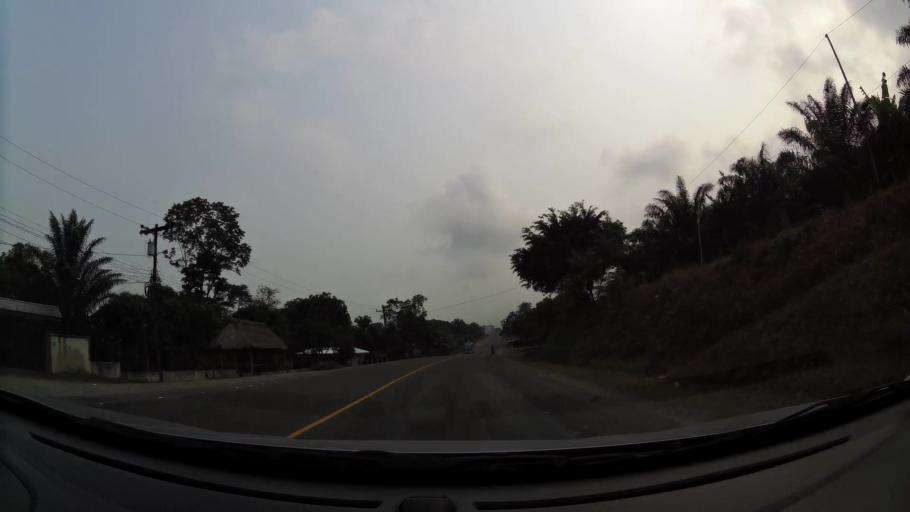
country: HN
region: Atlantida
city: Mezapa
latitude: 15.5716
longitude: -87.6182
